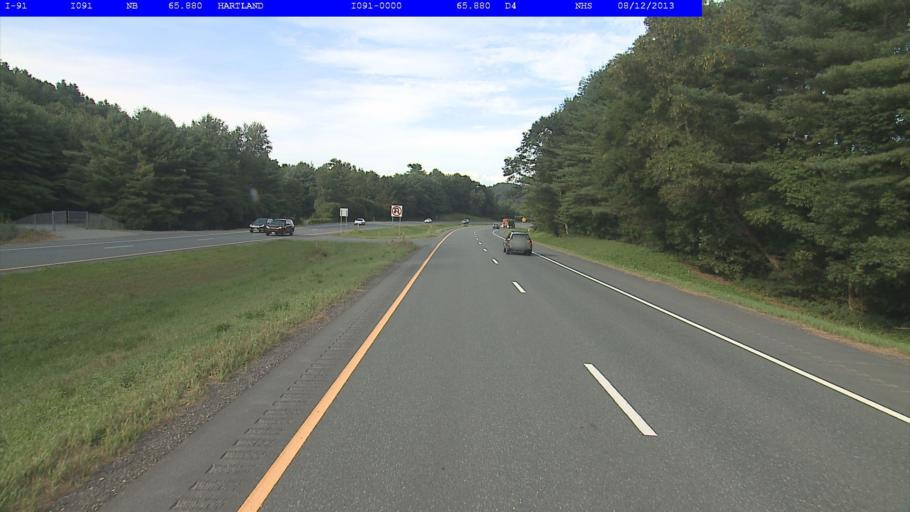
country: US
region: Vermont
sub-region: Windsor County
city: White River Junction
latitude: 43.5910
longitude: -72.3583
